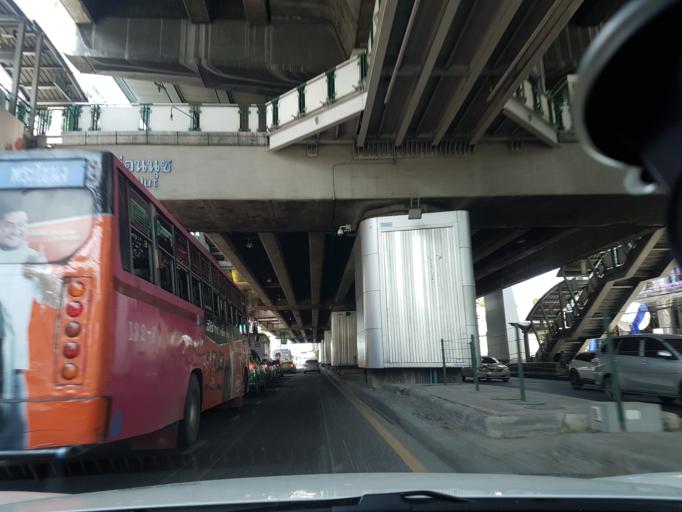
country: TH
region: Bangkok
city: Phra Khanong
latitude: 13.7052
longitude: 100.6011
